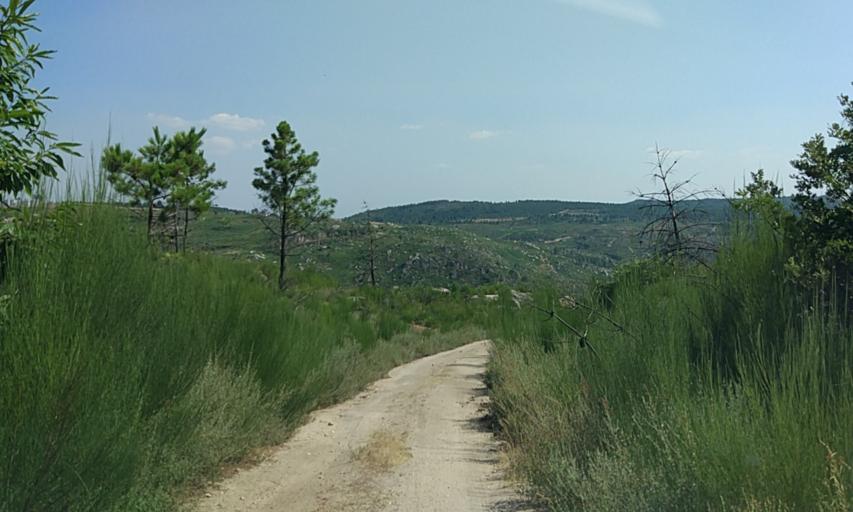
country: PT
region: Vila Real
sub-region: Murca
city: Murca
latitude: 41.3164
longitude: -7.4921
